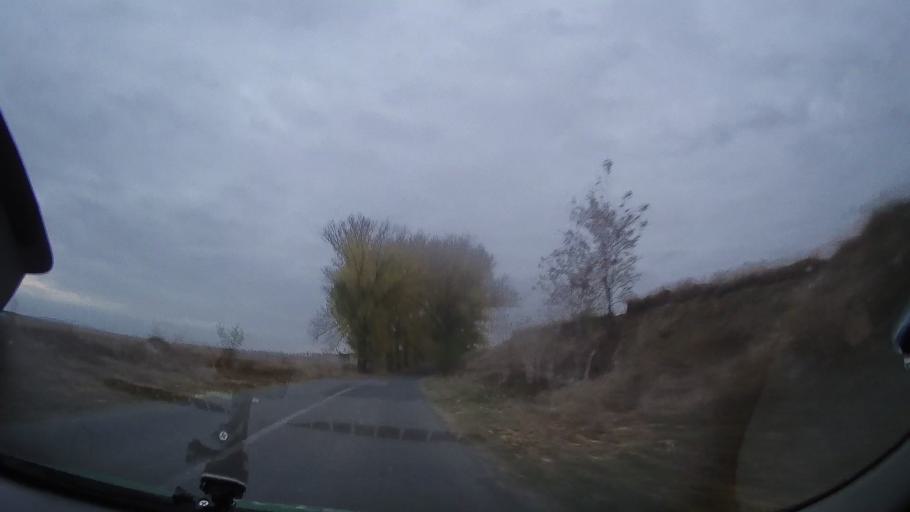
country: RO
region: Tulcea
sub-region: Comuna Mihai Bravu
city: Turda
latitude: 44.9658
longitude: 28.6342
